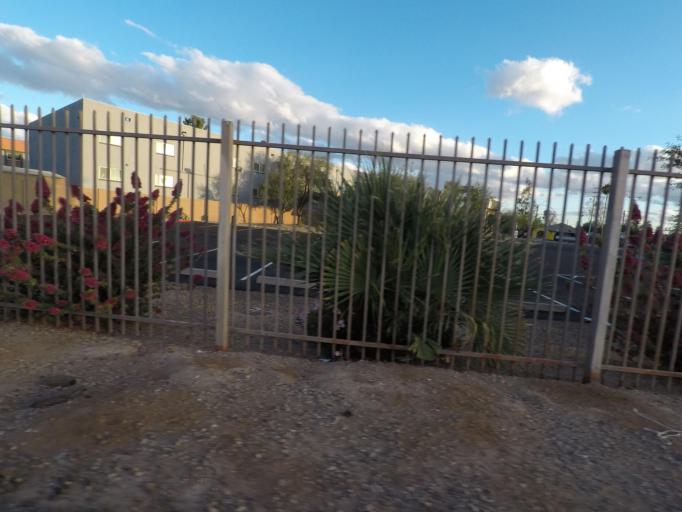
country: US
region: Arizona
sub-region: Maricopa County
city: Phoenix
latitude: 33.4957
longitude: -112.1062
